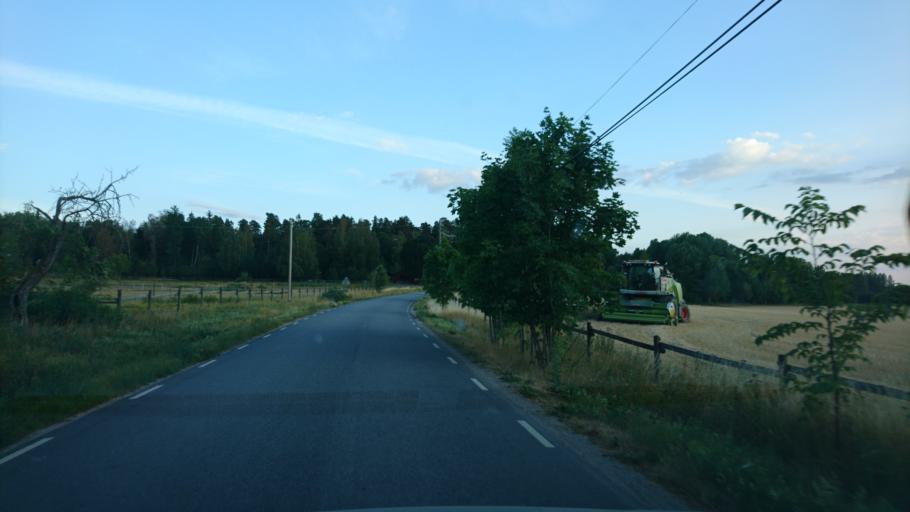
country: SE
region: Uppsala
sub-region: Uppsala Kommun
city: Saevja
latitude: 59.8123
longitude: 17.6803
